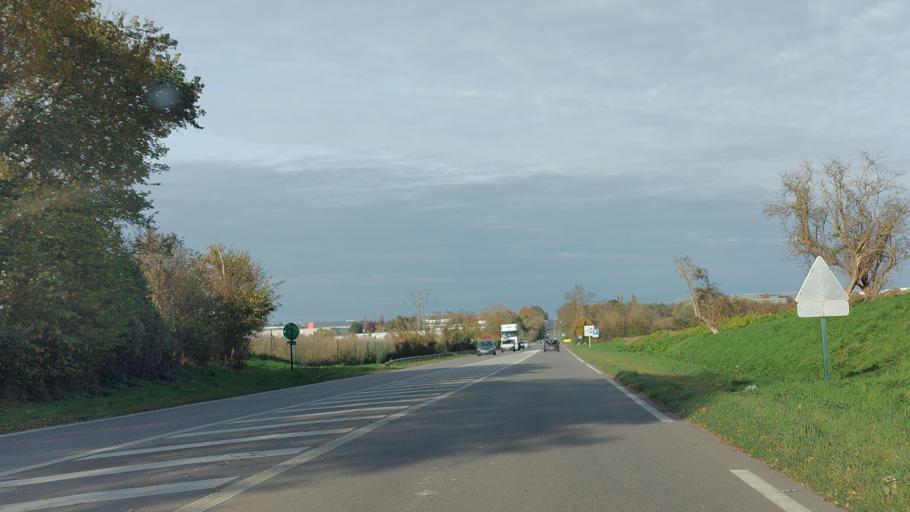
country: FR
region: Ile-de-France
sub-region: Departement du Val-d'Oise
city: Survilliers
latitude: 49.0802
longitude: 2.5295
